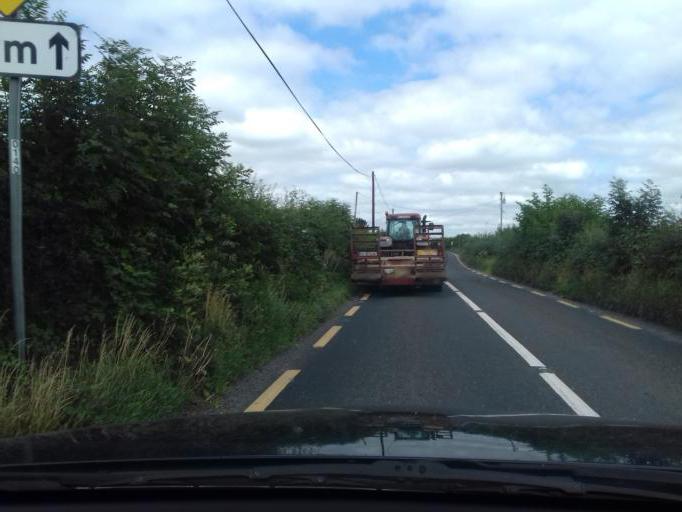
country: IE
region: Leinster
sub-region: County Carlow
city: Tullow
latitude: 52.8264
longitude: -6.7223
